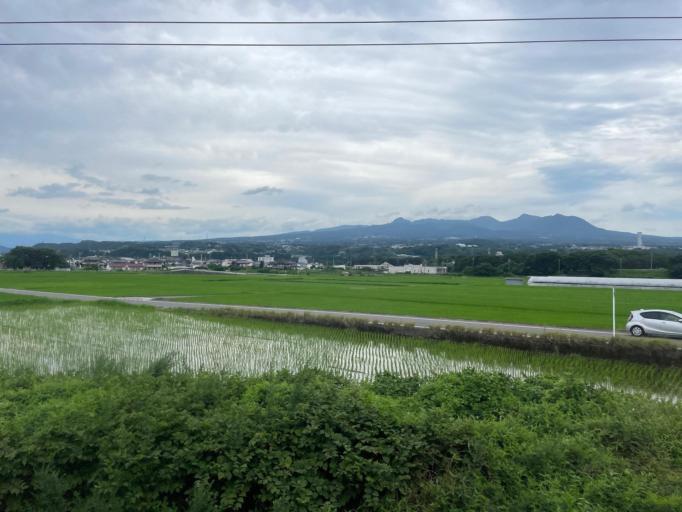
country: JP
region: Gunma
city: Shibukawa
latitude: 36.4750
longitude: 139.0102
